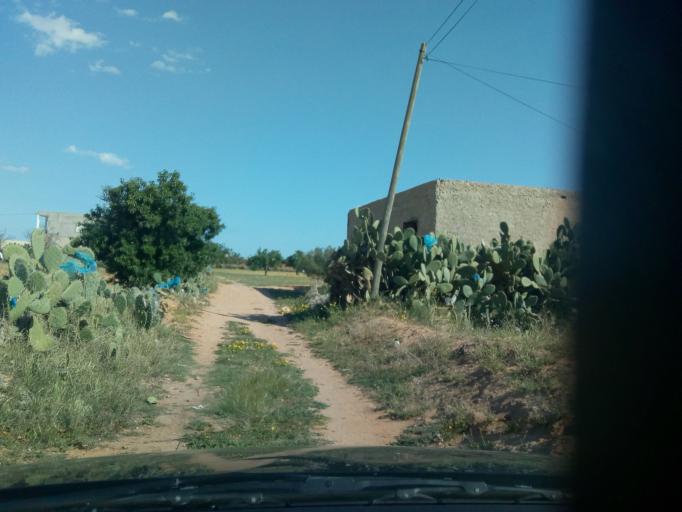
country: TN
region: Safaqis
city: Sfax
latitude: 34.7268
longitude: 10.6017
